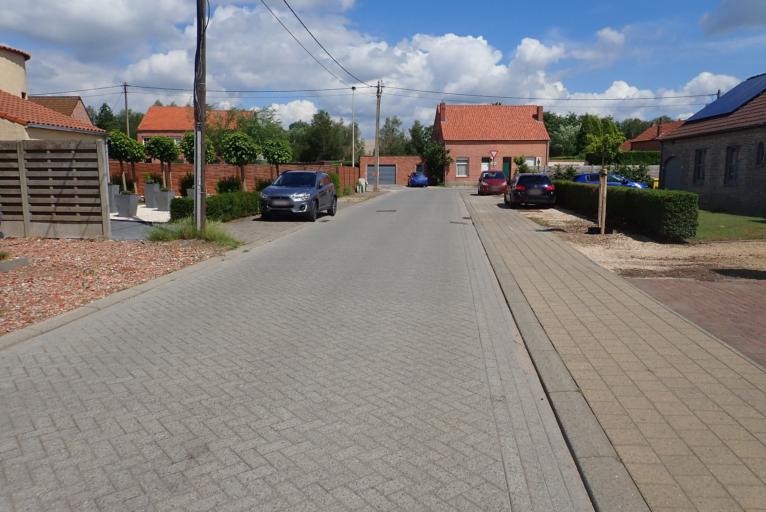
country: BE
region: Flanders
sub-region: Provincie Antwerpen
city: Beerse
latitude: 51.3229
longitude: 4.8253
